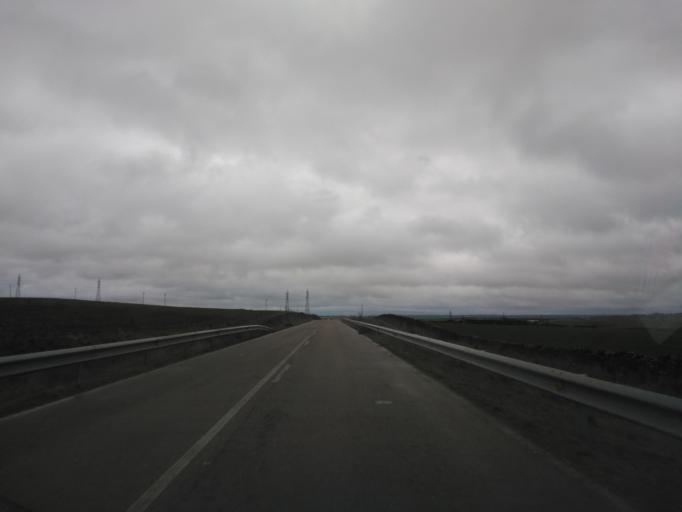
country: ES
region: Castille and Leon
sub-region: Provincia de Salamanca
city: Villamayor
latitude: 40.9663
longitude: -5.7075
